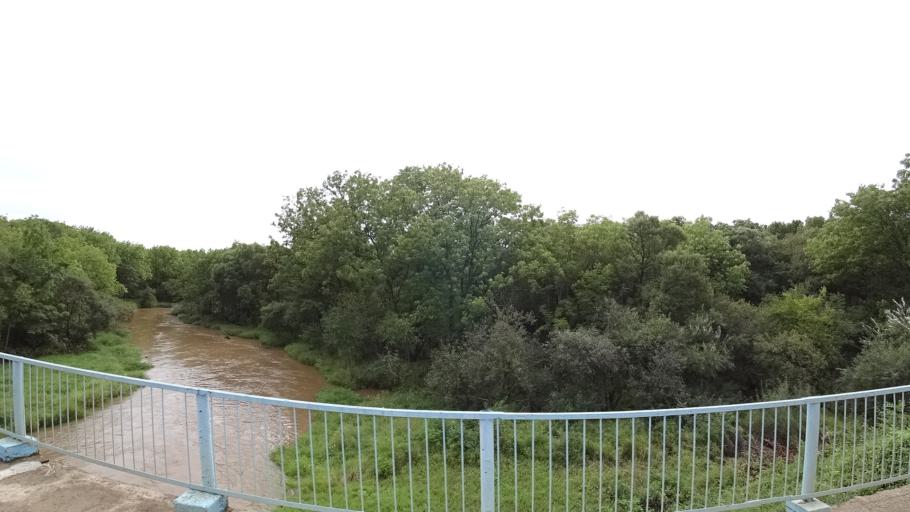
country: RU
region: Primorskiy
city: Lyalichi
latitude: 44.0822
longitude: 132.4481
